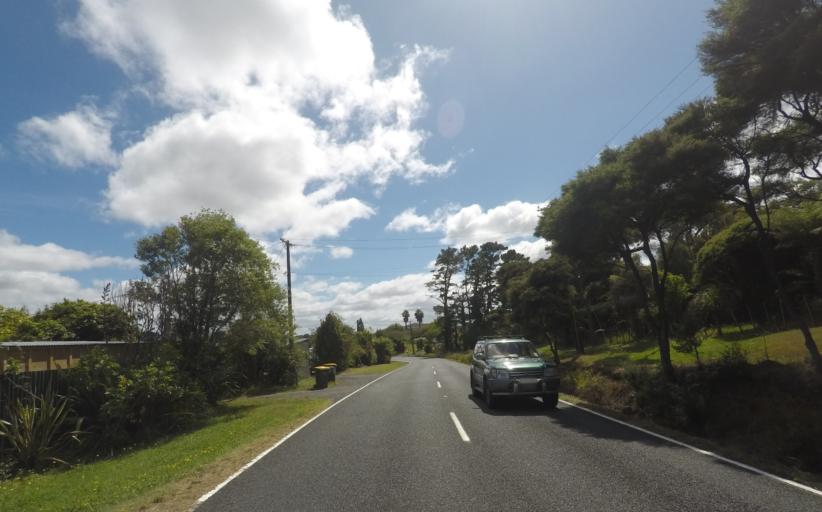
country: NZ
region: Auckland
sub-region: Auckland
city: Muriwai Beach
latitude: -36.8545
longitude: 174.5278
